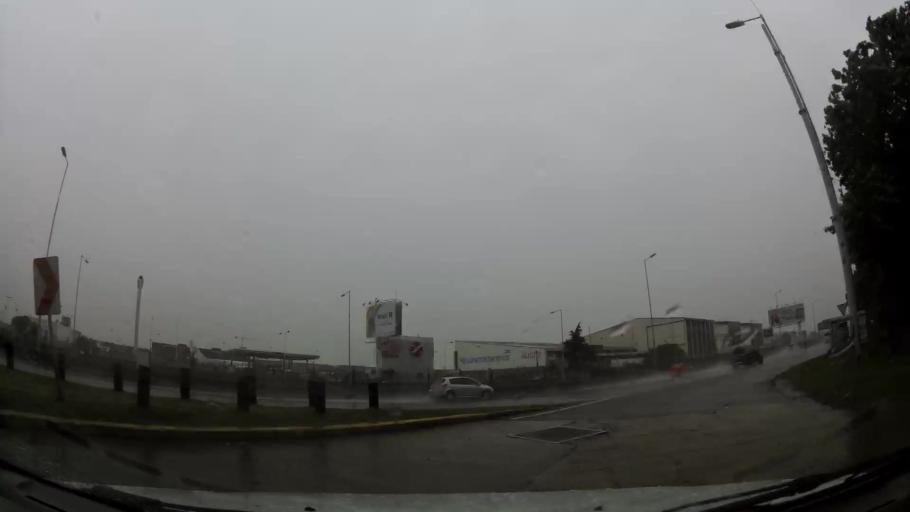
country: AR
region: Buenos Aires F.D.
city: Colegiales
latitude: -34.5627
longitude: -58.4166
